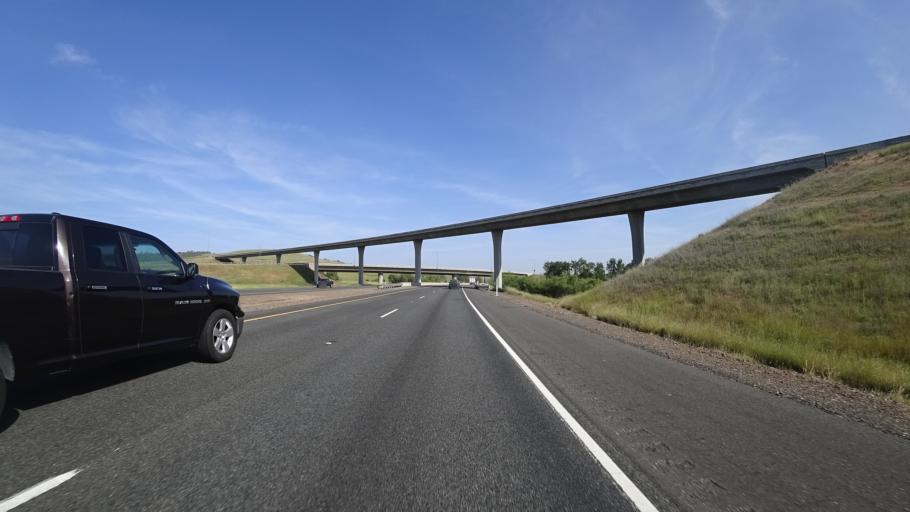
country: US
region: California
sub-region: Butte County
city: Thermalito
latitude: 39.5835
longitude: -121.6246
